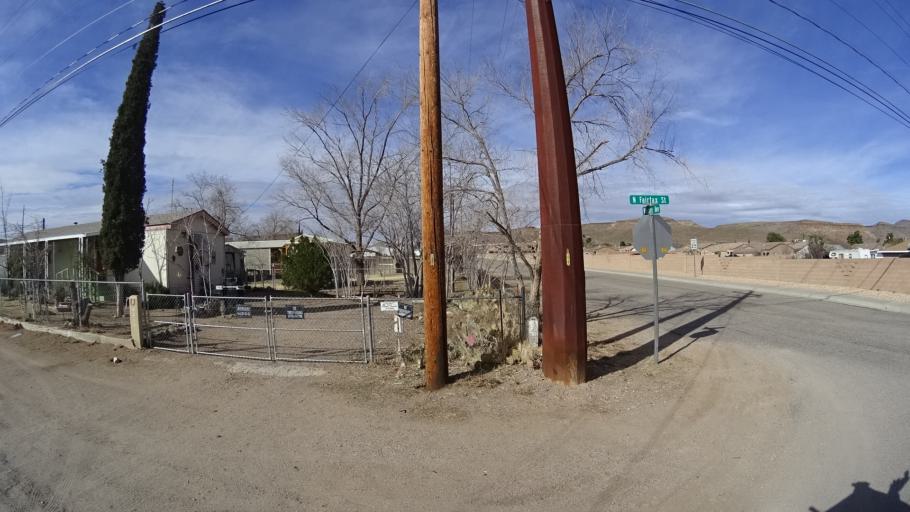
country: US
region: Arizona
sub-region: Mohave County
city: Kingman
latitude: 35.2185
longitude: -114.0446
